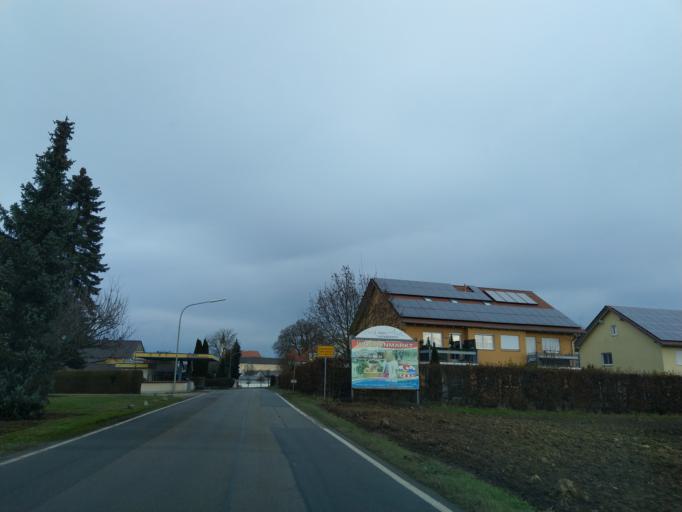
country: DE
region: Bavaria
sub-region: Lower Bavaria
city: Osterhofen
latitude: 48.6869
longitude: 13.0097
